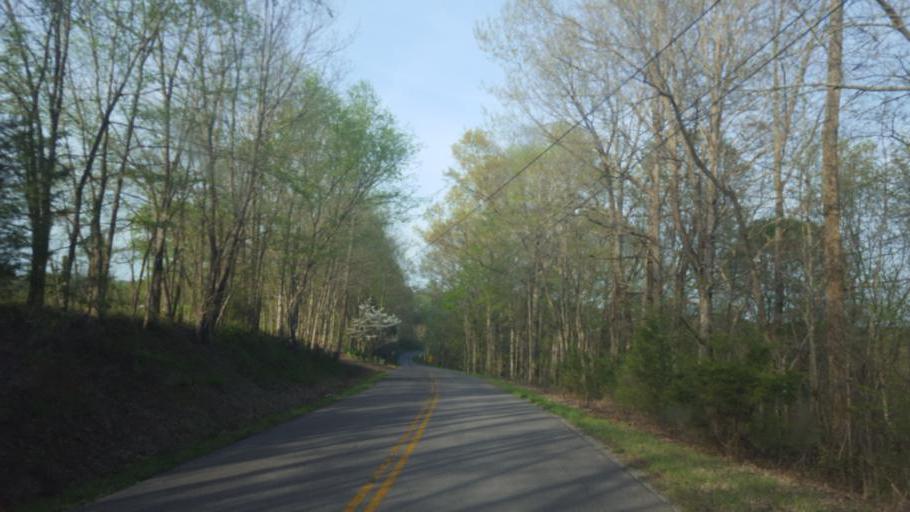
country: US
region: Kentucky
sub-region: Allen County
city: Scottsville
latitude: 36.8871
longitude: -86.1503
